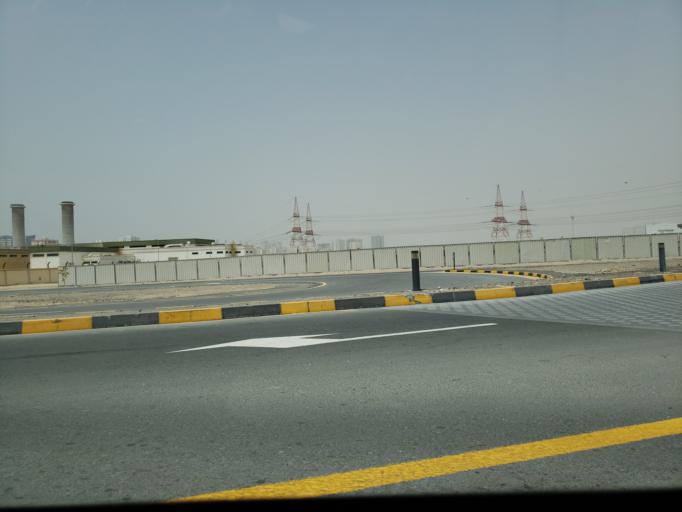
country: AE
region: Ajman
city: Ajman
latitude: 25.3692
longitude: 55.4626
